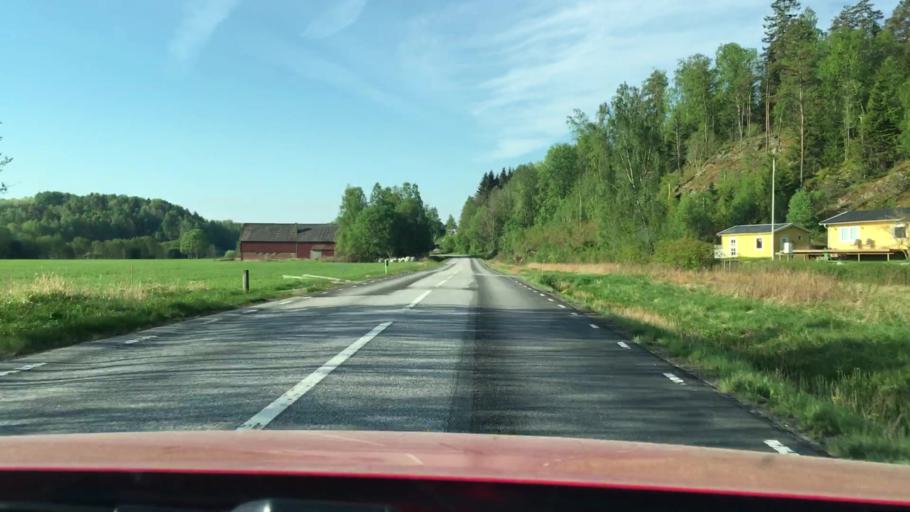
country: SE
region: Vaestra Goetaland
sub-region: Munkedals Kommun
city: Munkedal
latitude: 58.6237
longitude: 11.5596
